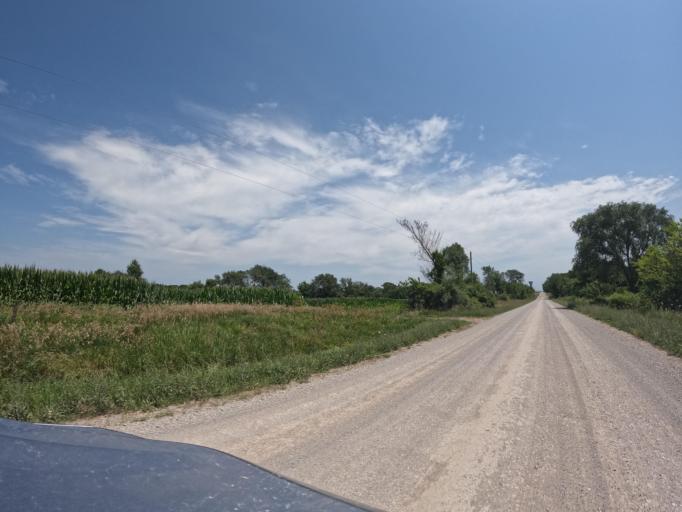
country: US
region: Iowa
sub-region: Appanoose County
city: Centerville
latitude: 40.7867
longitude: -92.9282
